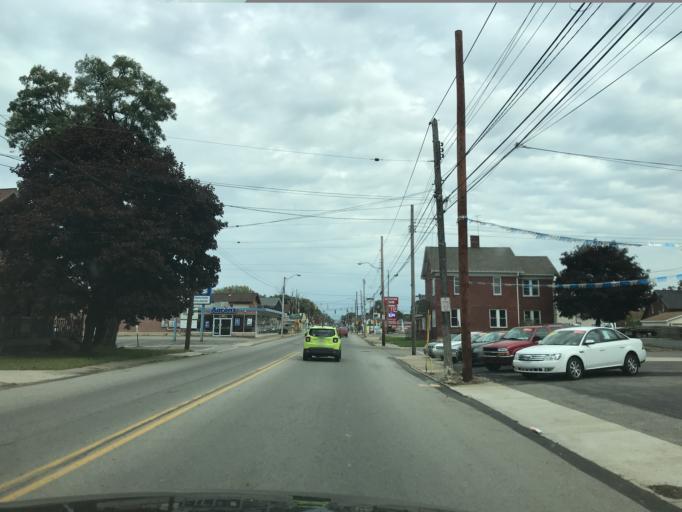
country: US
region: Pennsylvania
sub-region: Erie County
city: Wesleyville
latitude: 42.1384
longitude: -80.0190
